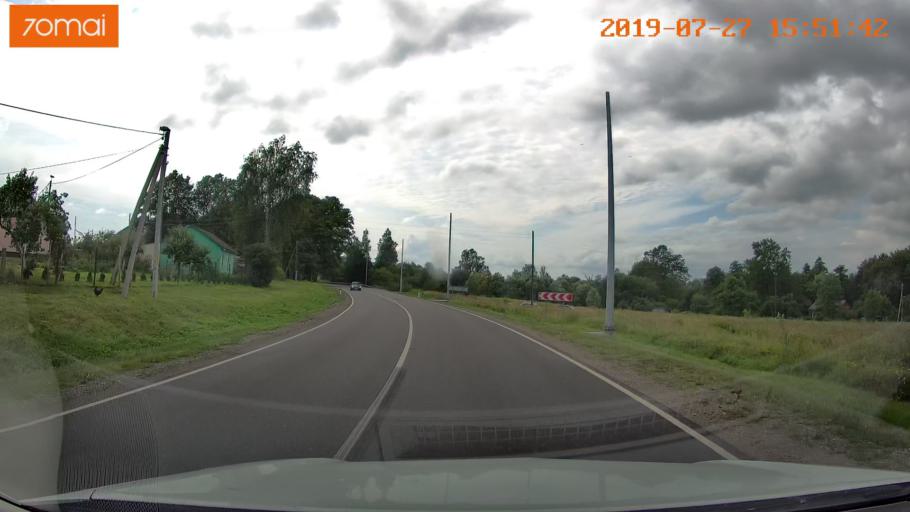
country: RU
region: Kaliningrad
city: Chernyakhovsk
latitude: 54.6028
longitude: 21.9745
